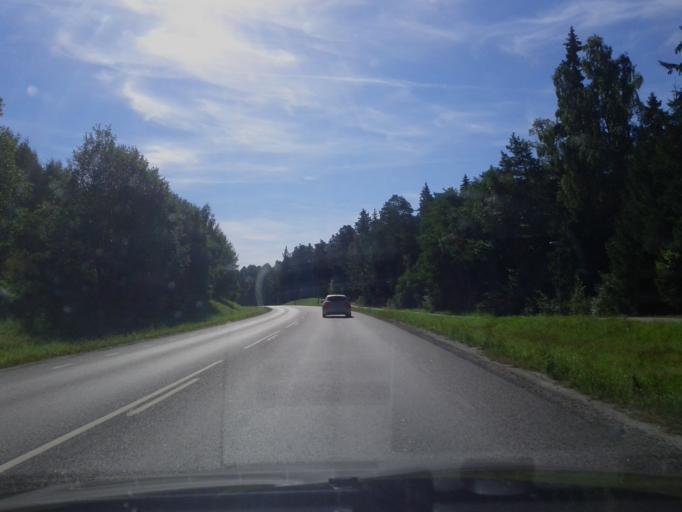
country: SE
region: Stockholm
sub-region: Taby Kommun
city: Taby
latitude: 59.4593
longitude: 18.0778
